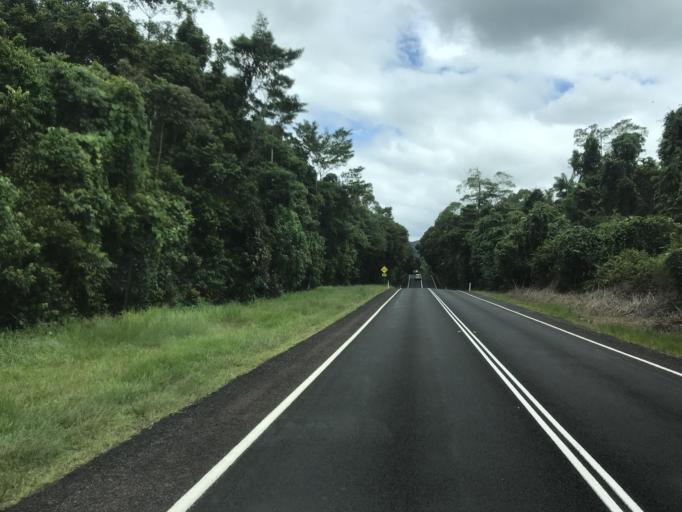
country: AU
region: Queensland
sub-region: Cassowary Coast
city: Innisfail
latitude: -17.8589
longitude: 146.0653
